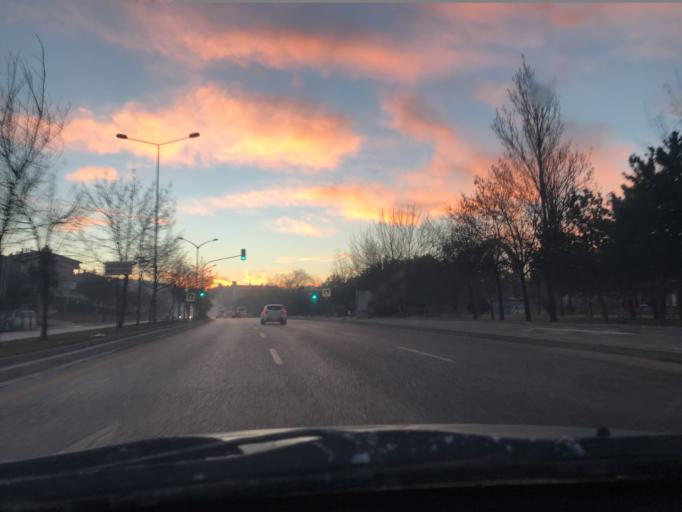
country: TR
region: Ankara
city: Batikent
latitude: 39.9655
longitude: 32.7349
